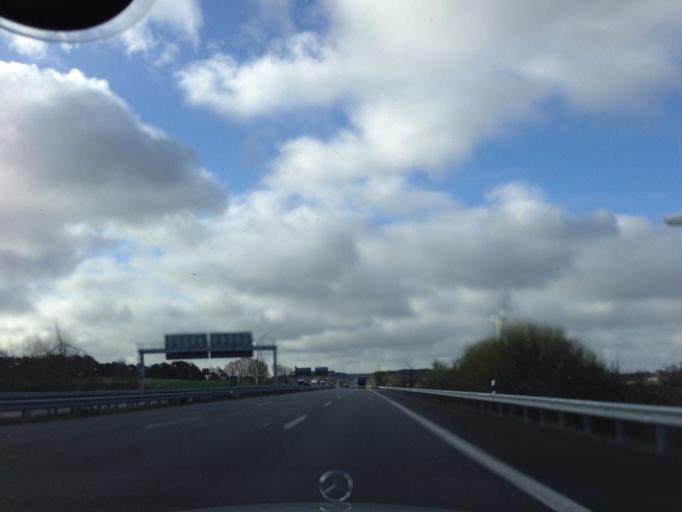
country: DE
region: Lower Saxony
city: Marxen
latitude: 53.3608
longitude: 10.0367
